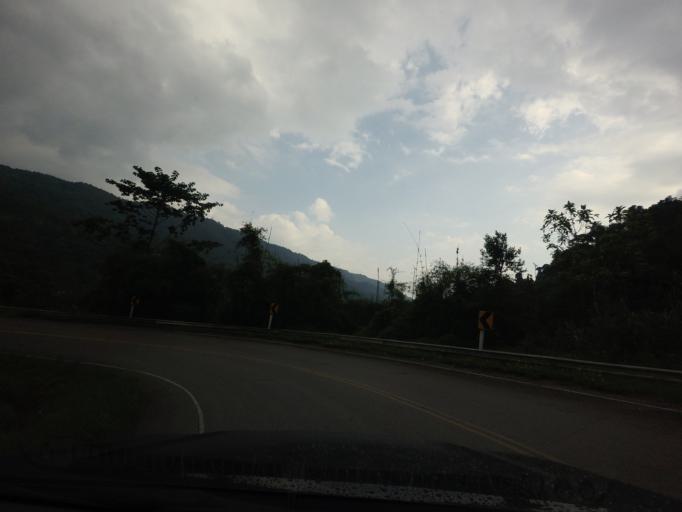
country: TH
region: Nan
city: Bo Kluea
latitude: 19.1492
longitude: 101.1507
